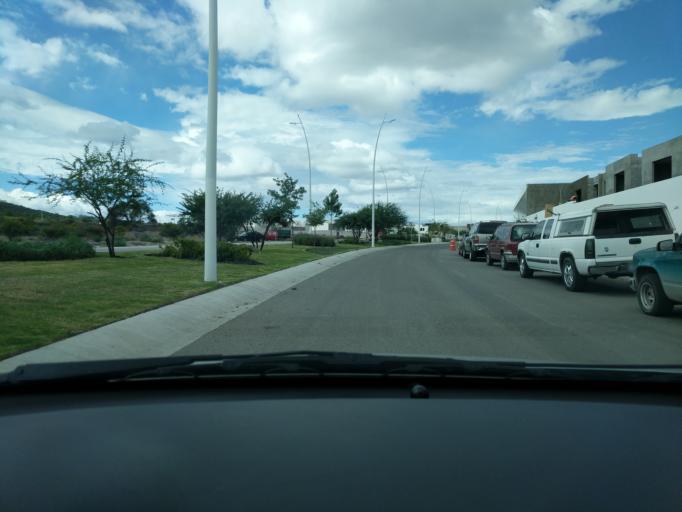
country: MX
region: Queretaro
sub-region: El Marques
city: La Pradera
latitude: 20.6611
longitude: -100.3167
